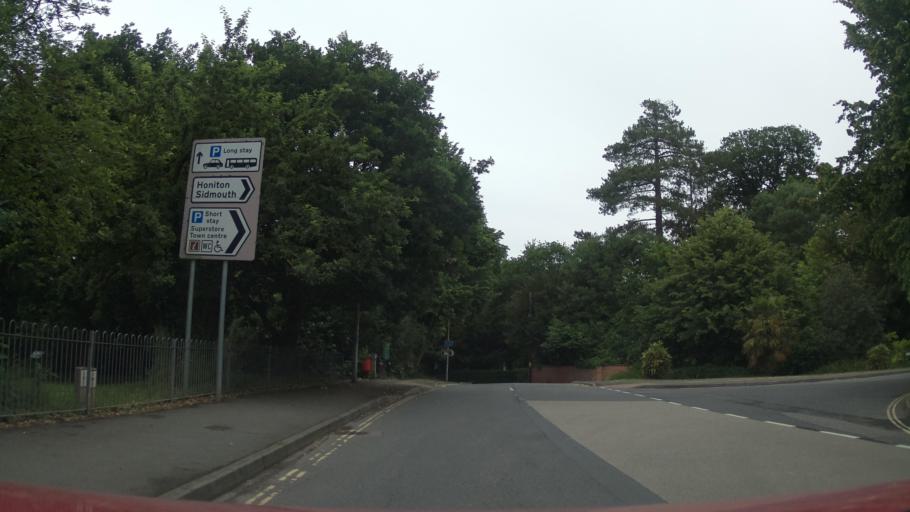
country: GB
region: England
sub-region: Devon
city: Ottery St Mary
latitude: 50.7518
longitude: -3.2830
